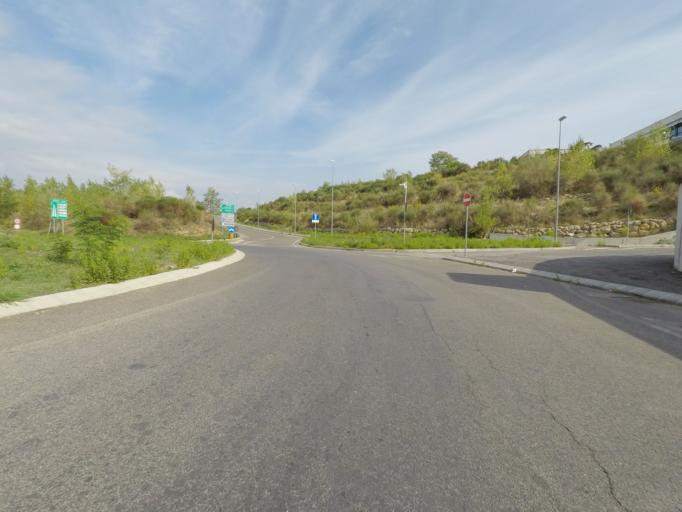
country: IT
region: Tuscany
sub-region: Provincia di Siena
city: Belverde
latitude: 43.3489
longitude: 11.3065
